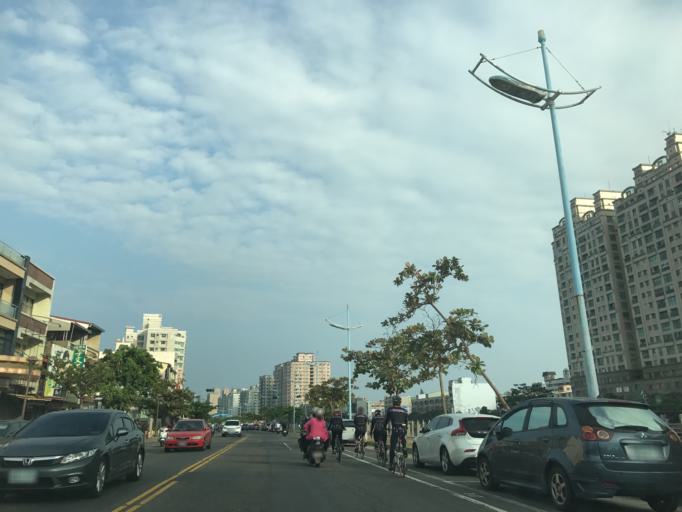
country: TW
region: Taiwan
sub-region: Tainan
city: Tainan
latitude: 22.9983
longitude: 120.1713
